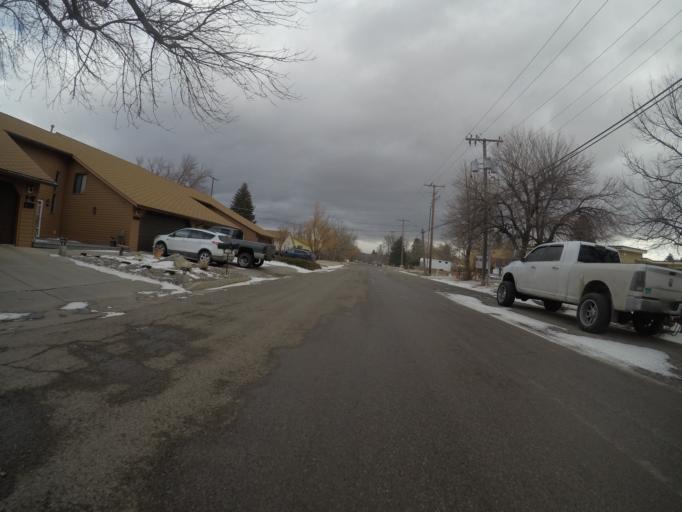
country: US
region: Montana
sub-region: Park County
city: Livingston
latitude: 45.6495
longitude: -110.5702
